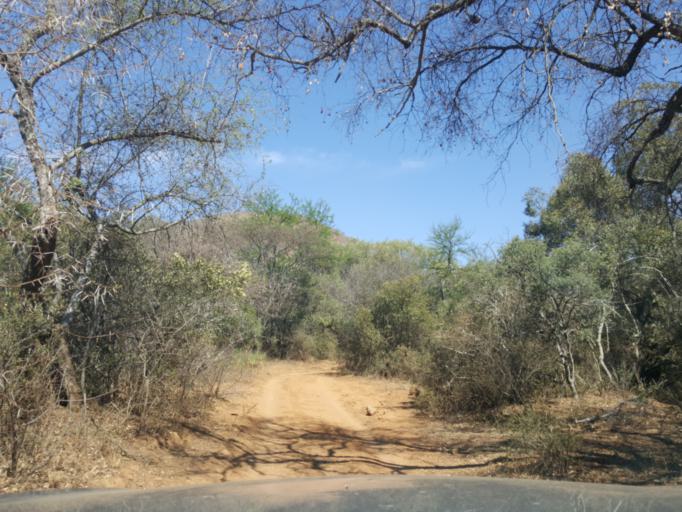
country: BW
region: South East
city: Lobatse
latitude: -25.1594
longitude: 25.6791
